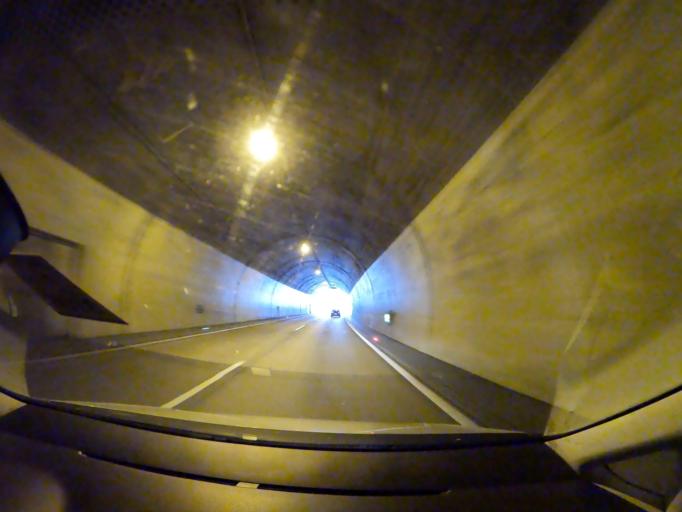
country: AT
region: Styria
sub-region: Politischer Bezirk Voitsberg
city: Modriach
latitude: 46.9800
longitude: 15.0886
